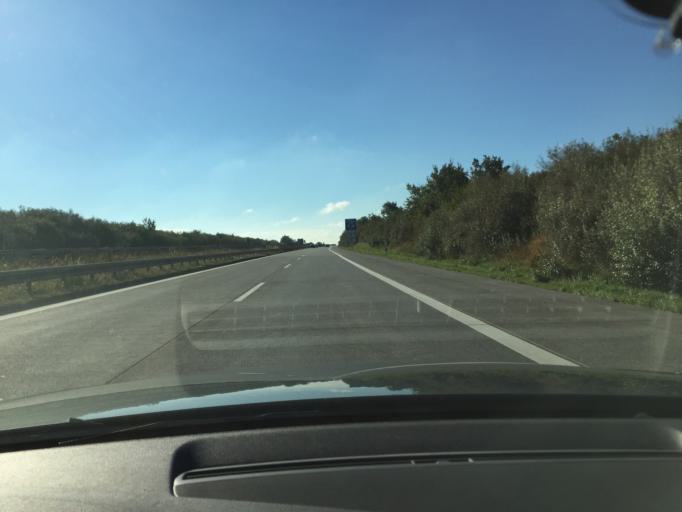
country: DE
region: Mecklenburg-Vorpommern
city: Laage
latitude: 53.8823
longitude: 12.2588
